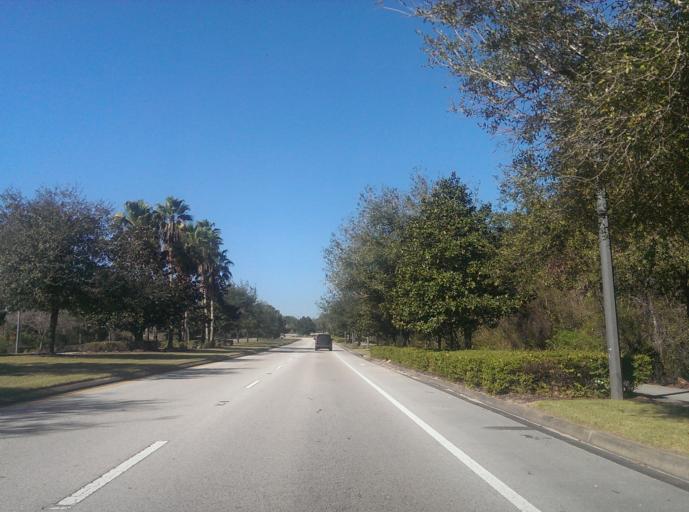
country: US
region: Florida
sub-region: Polk County
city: Loughman
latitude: 28.2598
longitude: -81.6032
